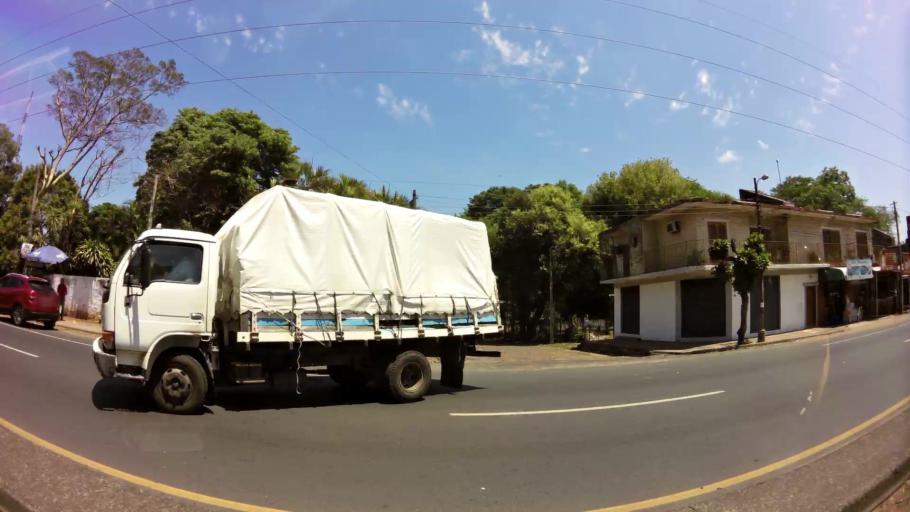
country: PY
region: Central
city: Villa Elisa
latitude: -25.3463
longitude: -57.5780
